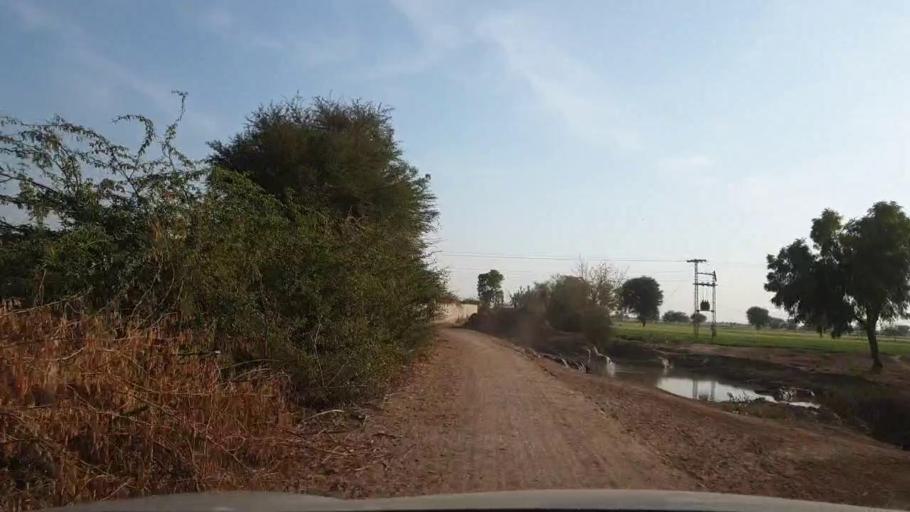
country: PK
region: Sindh
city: Berani
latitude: 25.7306
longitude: 68.7987
